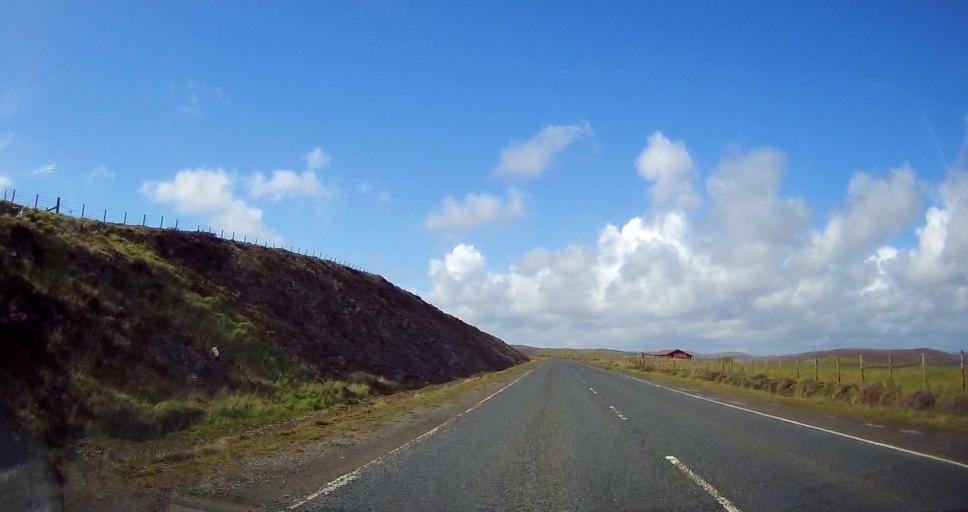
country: GB
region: Scotland
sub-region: Shetland Islands
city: Lerwick
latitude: 60.2205
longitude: -1.2342
